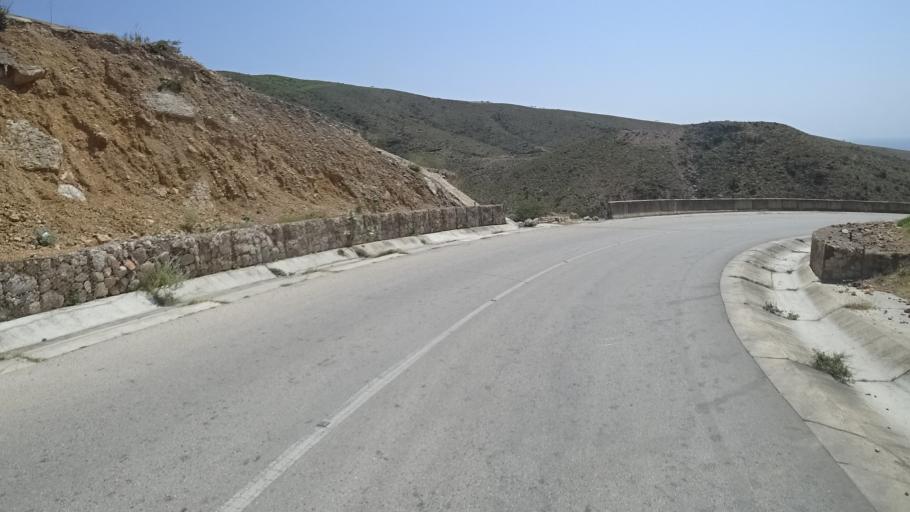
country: OM
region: Zufar
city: Salalah
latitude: 17.0470
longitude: 54.6131
